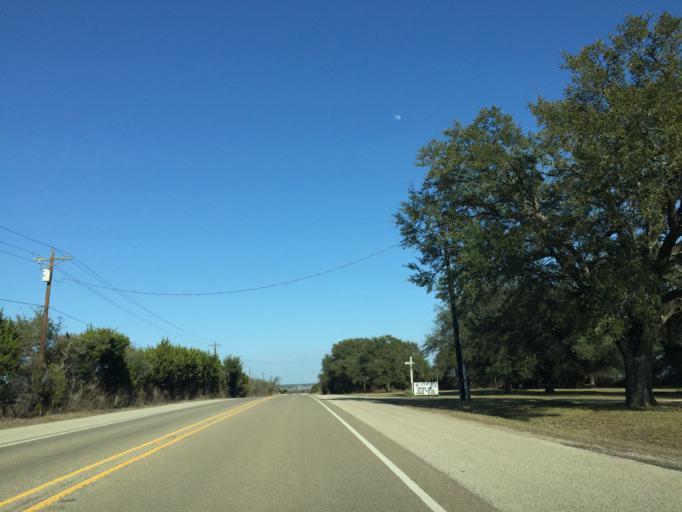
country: US
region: Texas
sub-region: Williamson County
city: Florence
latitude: 30.7693
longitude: -97.8280
